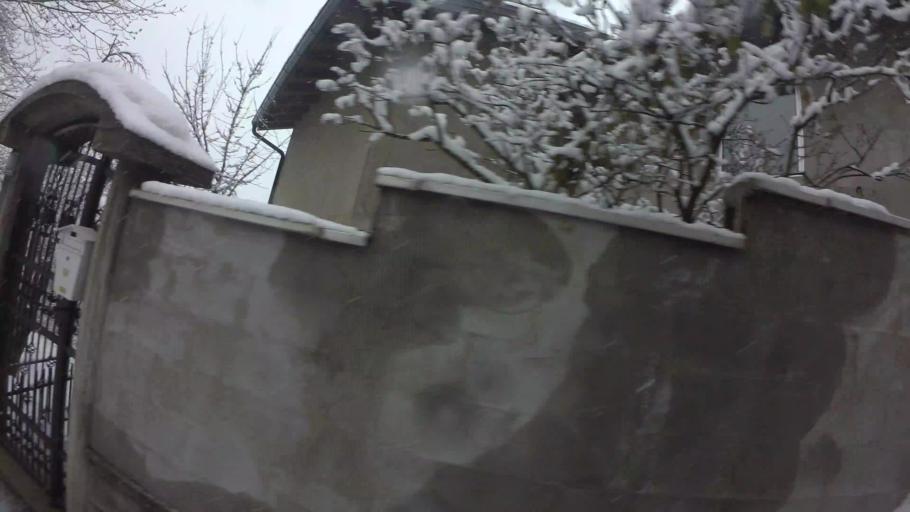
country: BA
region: Federation of Bosnia and Herzegovina
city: Kobilja Glava
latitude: 43.8502
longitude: 18.4394
